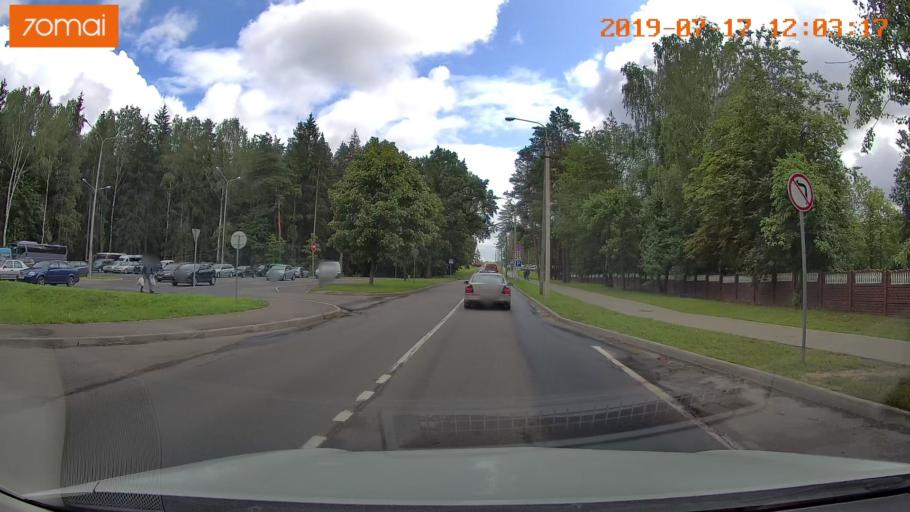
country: BY
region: Minsk
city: Lyasny
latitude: 54.0056
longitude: 27.6878
